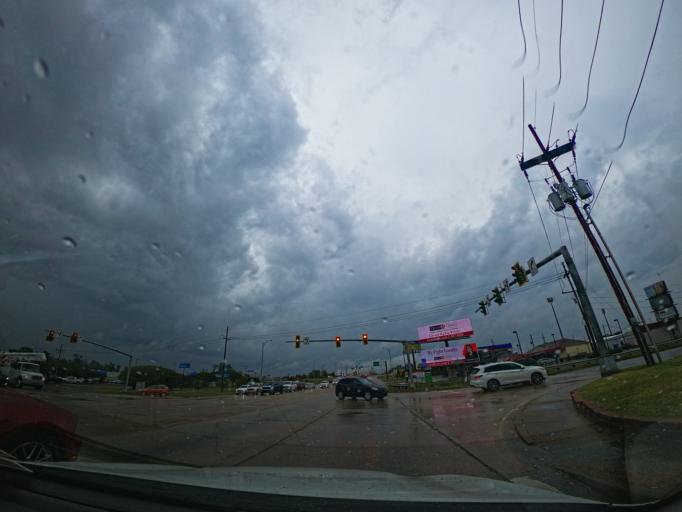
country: US
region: Louisiana
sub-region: Ouachita Parish
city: West Monroe
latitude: 32.5104
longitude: -92.1575
